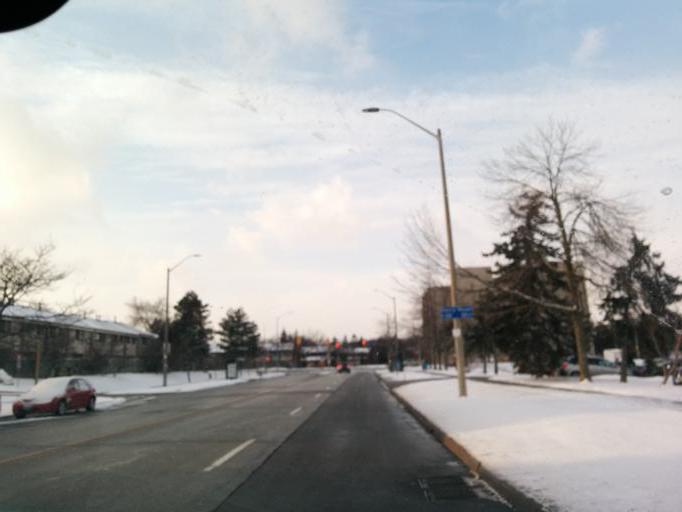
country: CA
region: Ontario
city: Brampton
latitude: 43.5923
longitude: -79.7642
